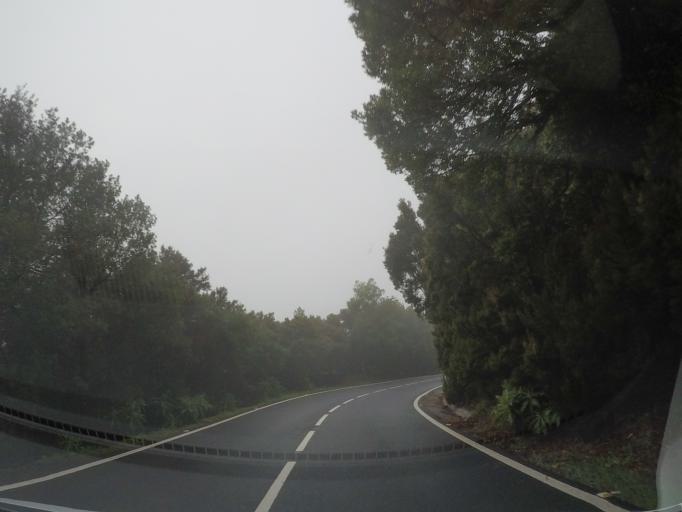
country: ES
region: Canary Islands
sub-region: Provincia de Santa Cruz de Tenerife
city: Alajero
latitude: 28.1115
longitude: -17.2405
